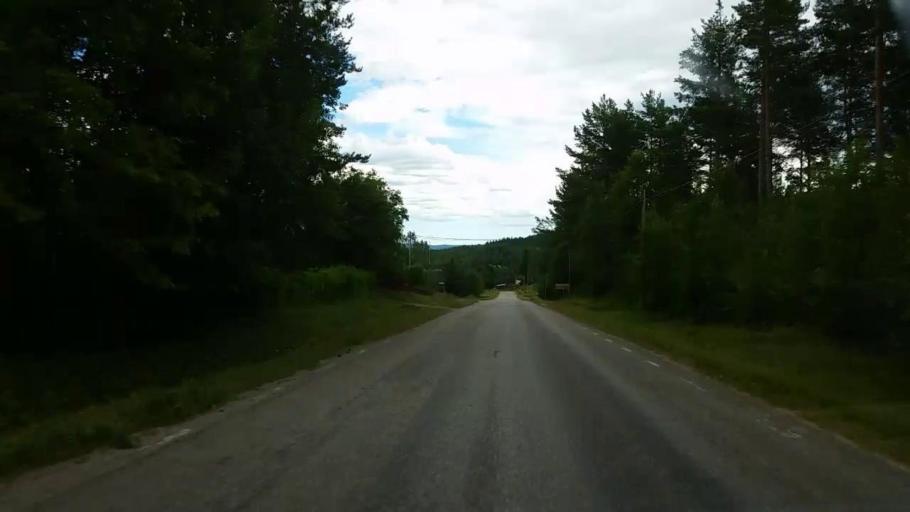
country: SE
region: Gaevleborg
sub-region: Ljusdals Kommun
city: Jaervsoe
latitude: 61.6683
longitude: 16.0763
